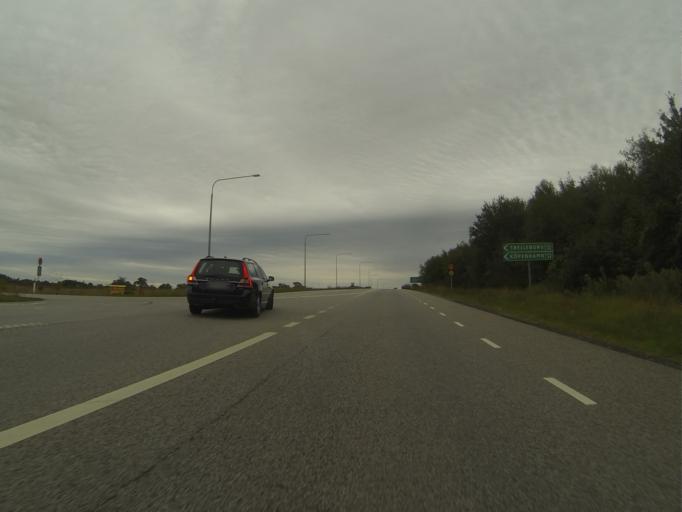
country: SE
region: Skane
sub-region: Malmo
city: Oxie
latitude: 55.5894
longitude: 13.1130
